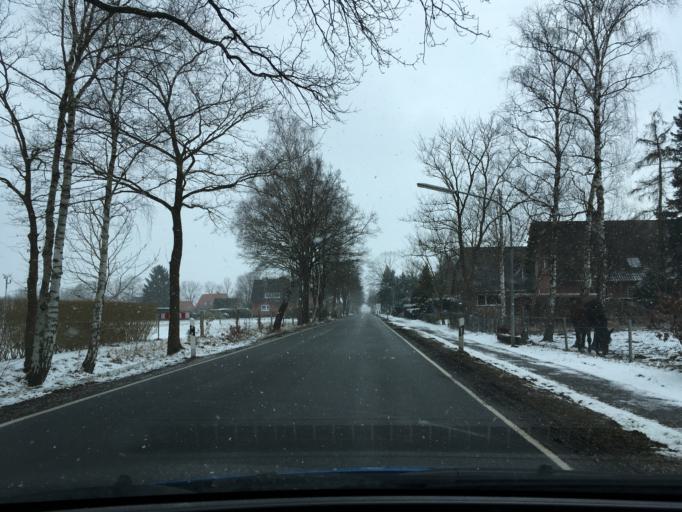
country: DE
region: Lower Saxony
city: Vierhofen
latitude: 53.2734
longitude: 10.2134
